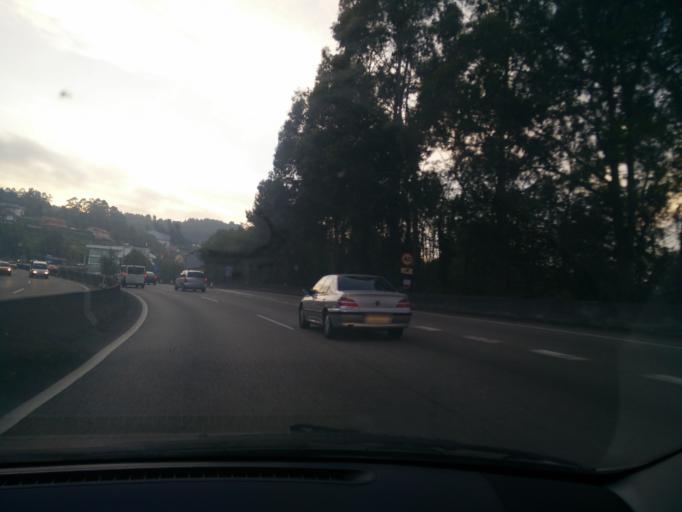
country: ES
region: Galicia
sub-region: Provincia de Pontevedra
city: Porrino
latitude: 42.1974
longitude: -8.6531
